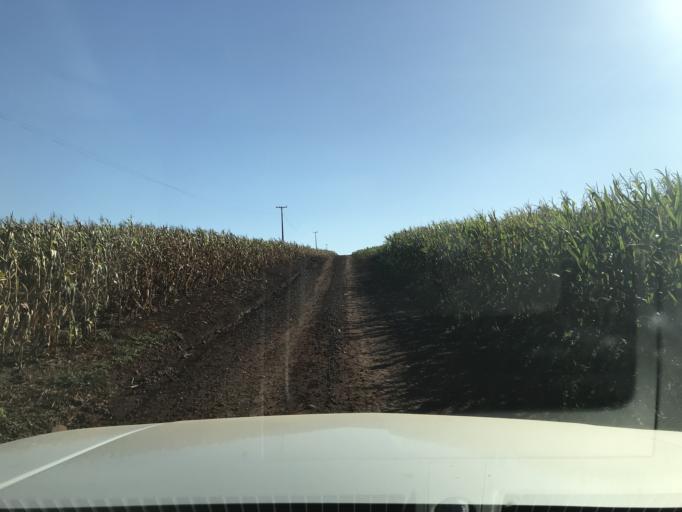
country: BR
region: Parana
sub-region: Palotina
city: Palotina
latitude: -24.2275
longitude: -53.8159
